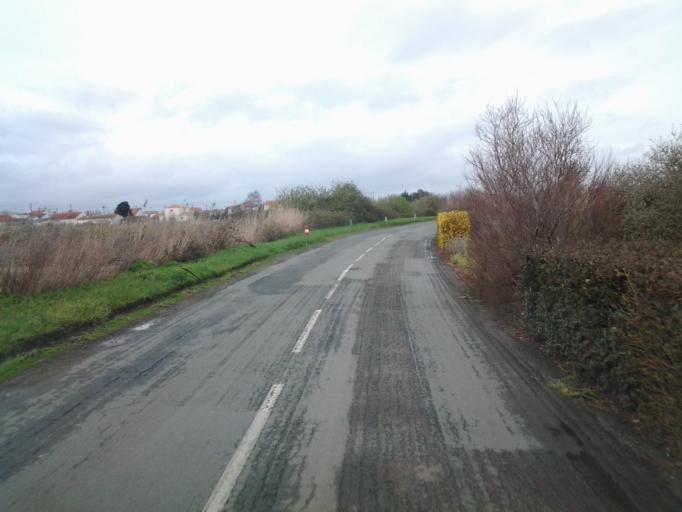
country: FR
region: Pays de la Loire
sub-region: Departement de la Vendee
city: La Tranche-sur-Mer
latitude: 46.3583
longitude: -1.4528
